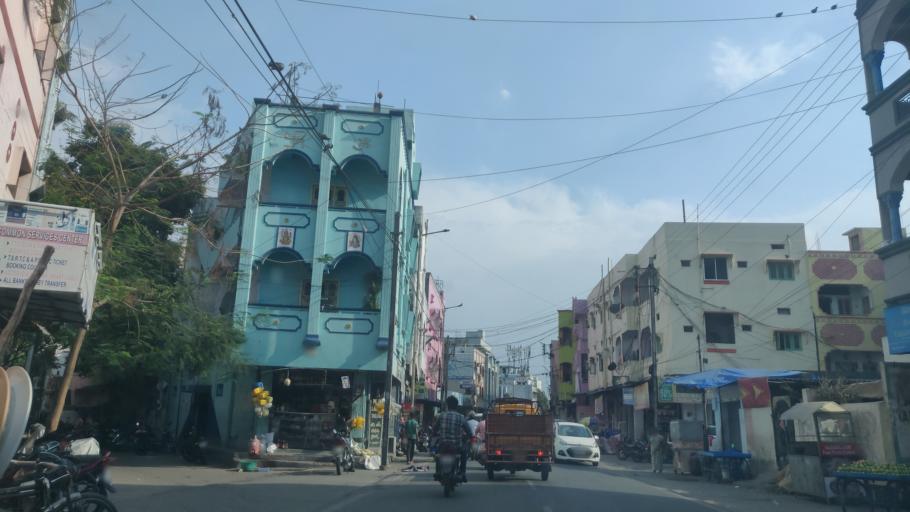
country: IN
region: Telangana
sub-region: Rangareddi
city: Gaddi Annaram
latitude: 17.3898
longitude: 78.5112
